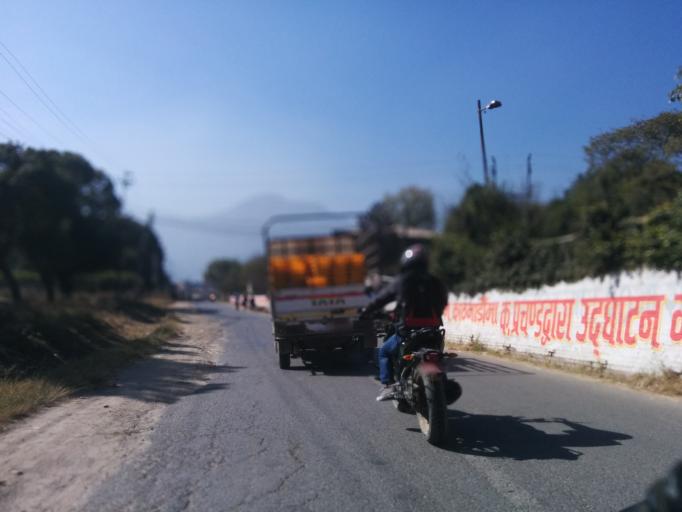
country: NP
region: Central Region
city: Kirtipur
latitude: 27.6783
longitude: 85.2849
